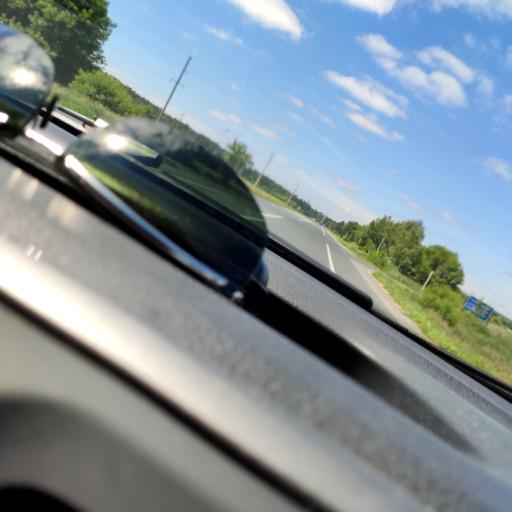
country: RU
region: Samara
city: Kurumoch
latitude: 53.4898
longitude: 49.9859
